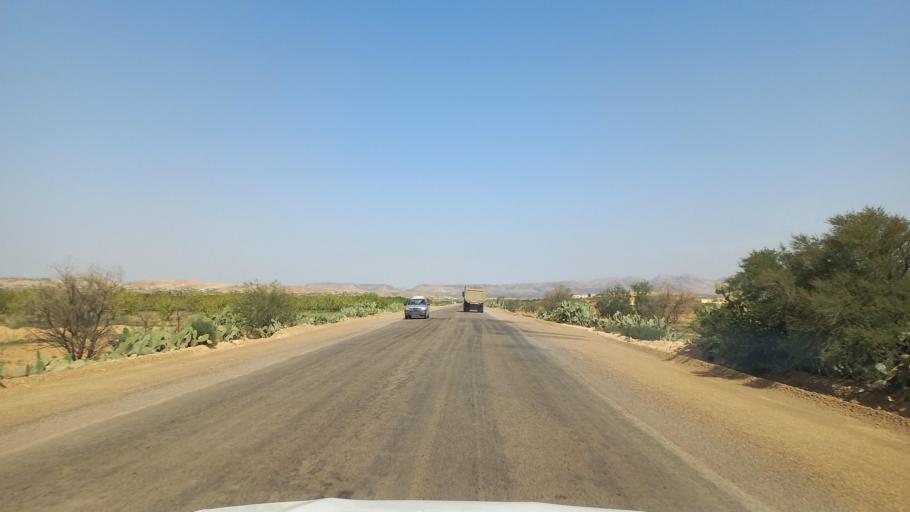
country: TN
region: Al Qasrayn
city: Sbiba
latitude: 35.3569
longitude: 9.0477
